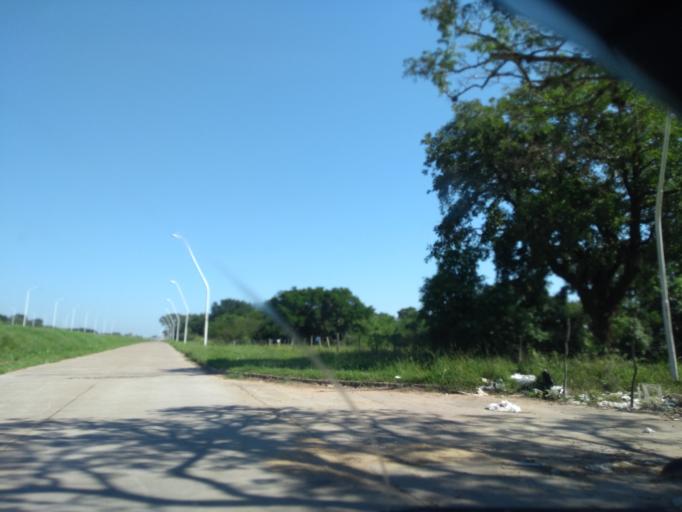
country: AR
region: Chaco
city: Barranqueras
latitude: -27.4337
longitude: -58.9242
